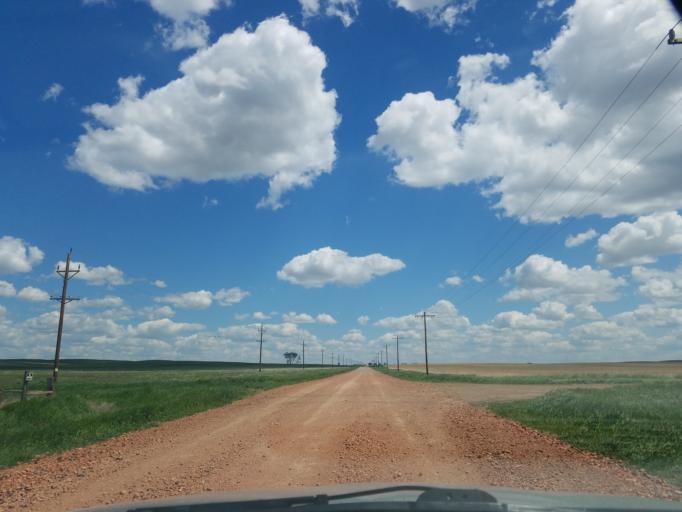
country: US
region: North Dakota
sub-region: McKenzie County
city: Watford City
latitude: 47.8194
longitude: -103.5838
